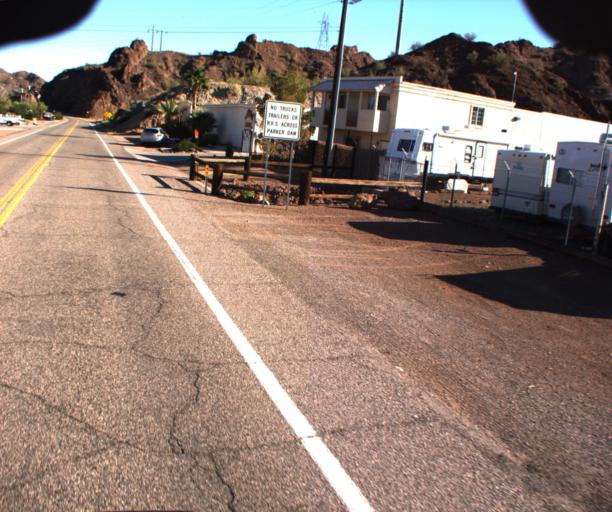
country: US
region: Arizona
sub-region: La Paz County
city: Cienega Springs
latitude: 34.2862
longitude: -114.1353
